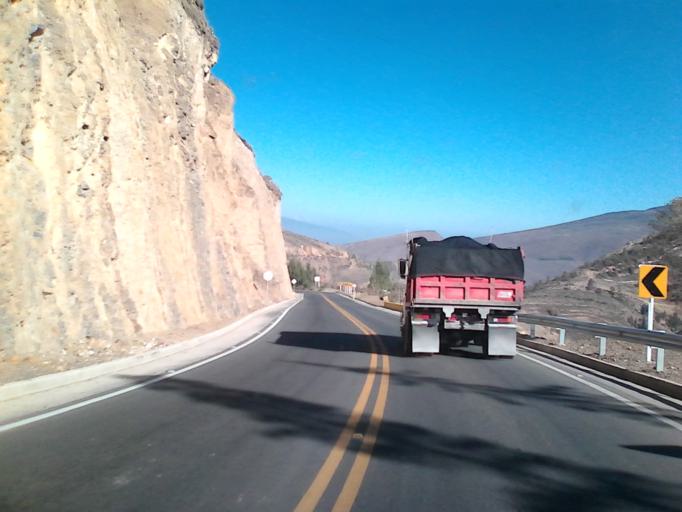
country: CO
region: Boyaca
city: Cucaita
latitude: 5.5549
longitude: -73.4955
